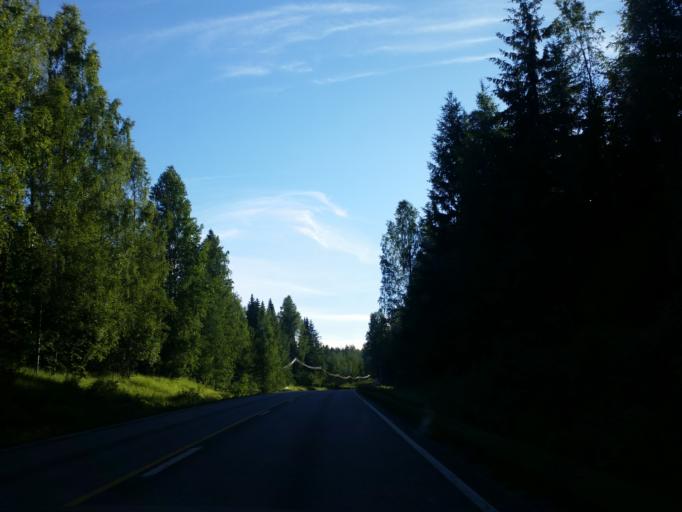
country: FI
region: Northern Savo
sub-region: Kuopio
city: Kuopio
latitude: 62.8444
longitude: 27.4178
